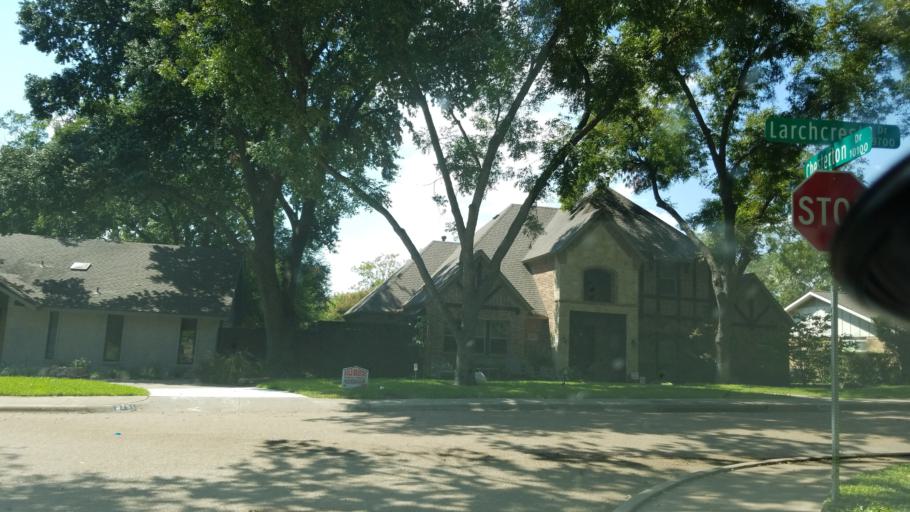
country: US
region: Texas
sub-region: Dallas County
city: Richardson
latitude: 32.8813
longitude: -96.7117
